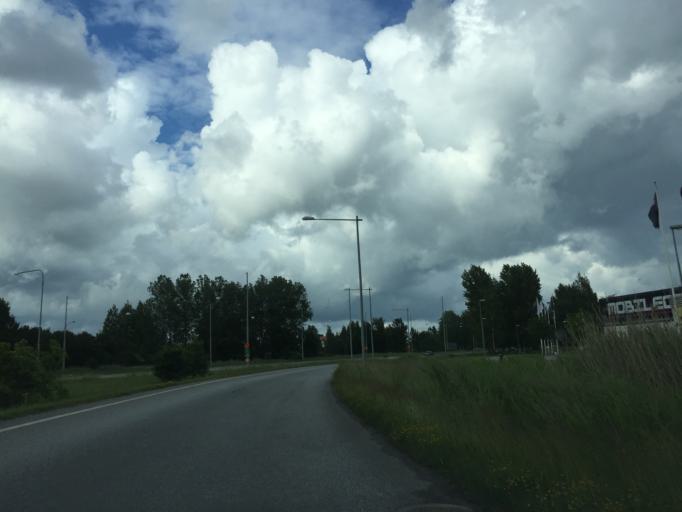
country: SE
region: OErebro
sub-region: Orebro Kommun
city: Orebro
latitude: 59.2623
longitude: 15.1780
